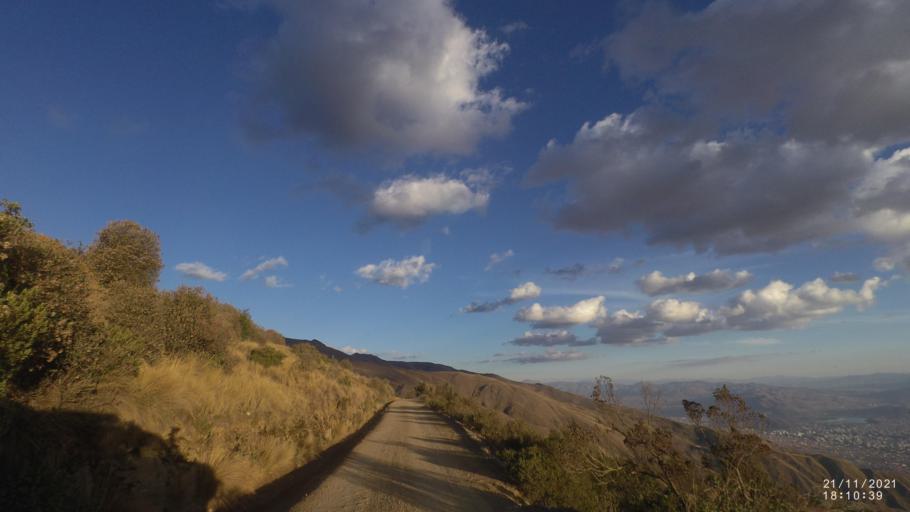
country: BO
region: Cochabamba
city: Cochabamba
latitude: -17.2876
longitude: -66.2137
